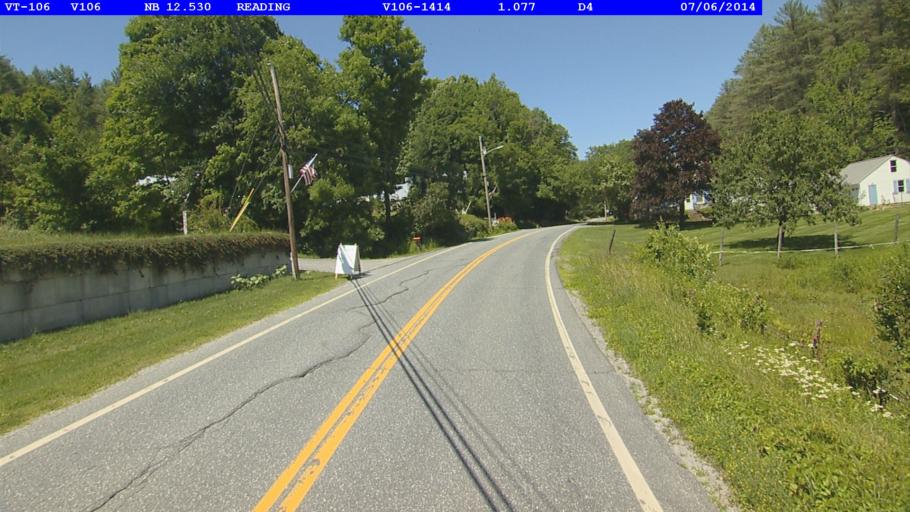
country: US
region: Vermont
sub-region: Windsor County
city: Windsor
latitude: 43.4597
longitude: -72.5370
